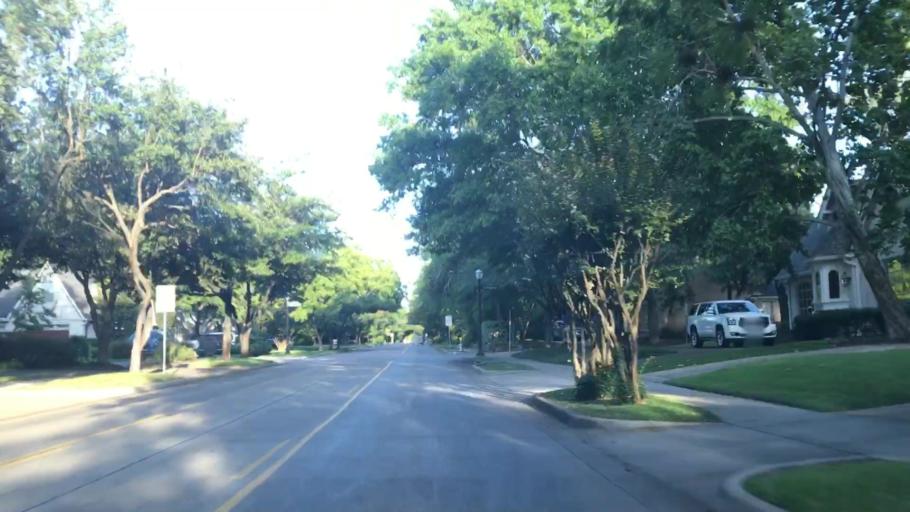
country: US
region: Texas
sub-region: Dallas County
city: University Park
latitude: 32.8511
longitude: -96.7856
